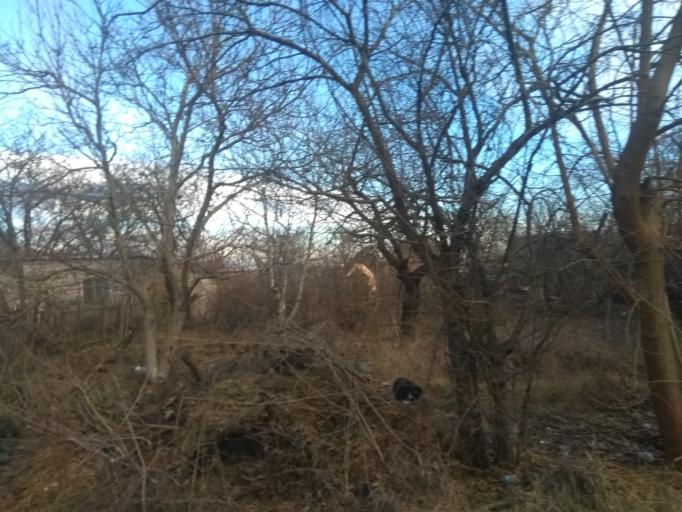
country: RU
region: Stavropol'skiy
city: Krasnokumskoye
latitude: 44.1774
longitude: 43.4791
